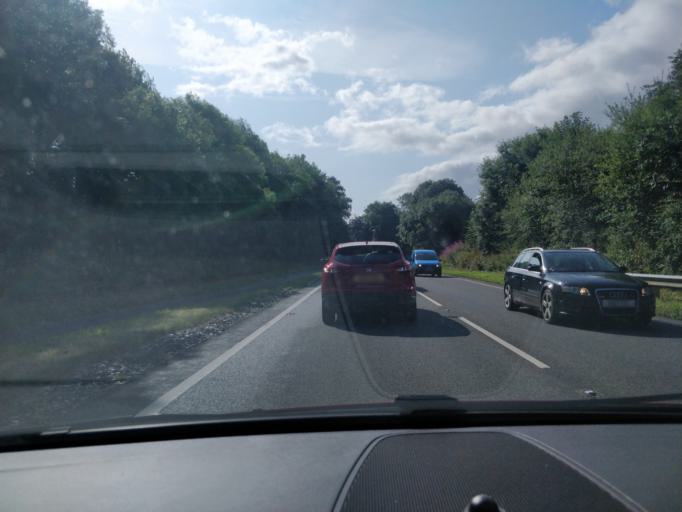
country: GB
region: Wales
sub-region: Conwy
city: Llanrwst
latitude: 53.1476
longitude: -3.8041
